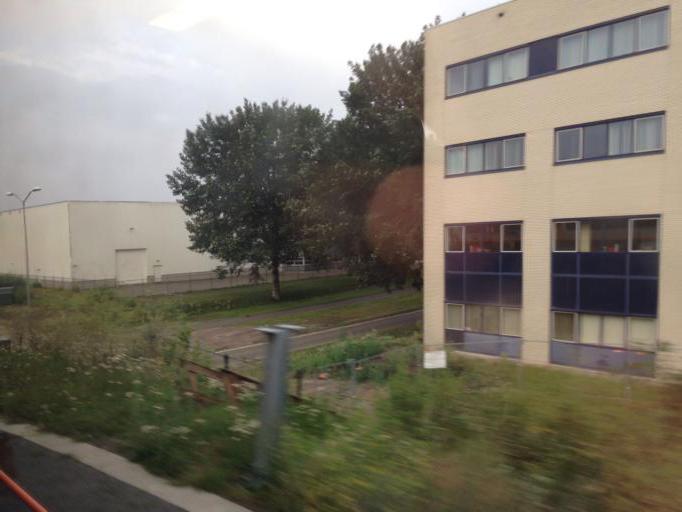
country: NL
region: Flevoland
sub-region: Gemeente Almere
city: Almere Stad
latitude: 52.3645
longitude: 5.1840
